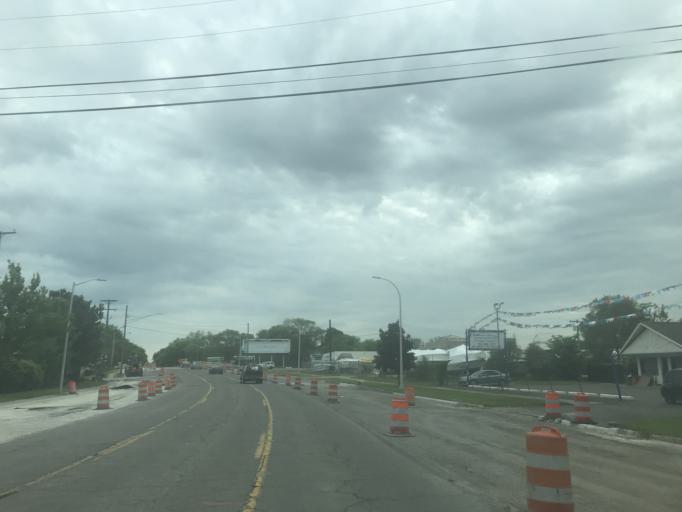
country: US
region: Michigan
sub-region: Wayne County
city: Ecorse
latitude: 42.2366
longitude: -83.1481
